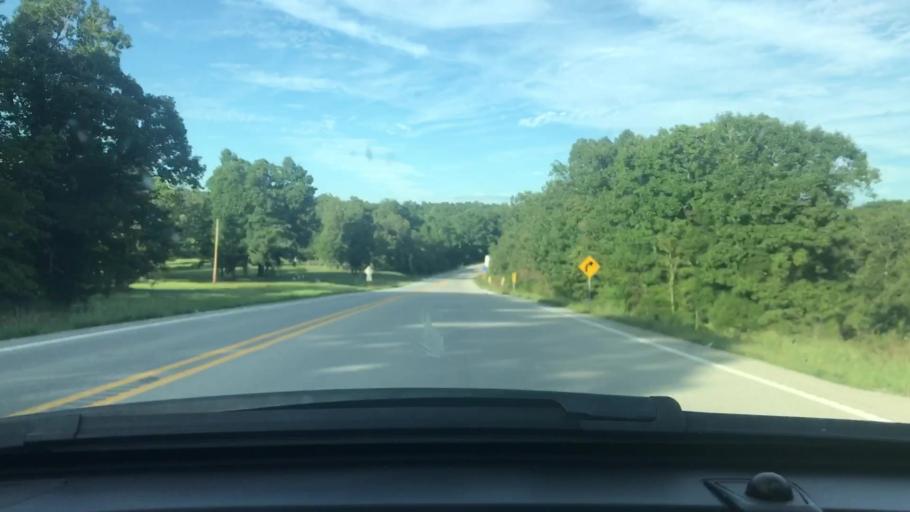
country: US
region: Arkansas
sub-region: Sharp County
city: Cherokee Village
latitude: 36.2750
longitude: -91.3168
